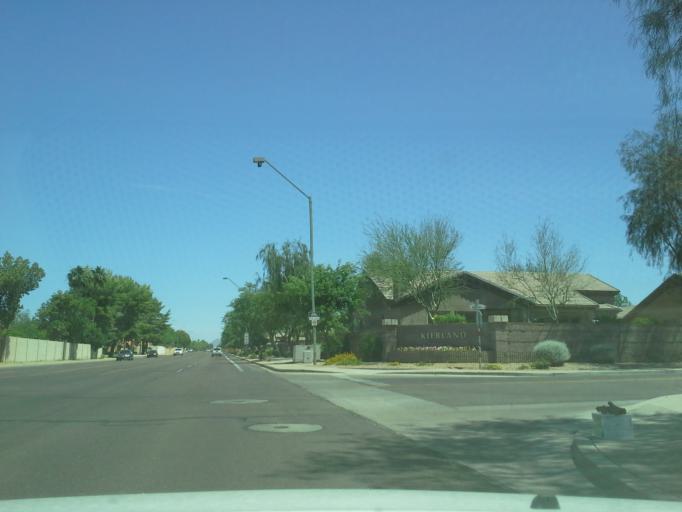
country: US
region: Arizona
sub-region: Maricopa County
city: Paradise Valley
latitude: 33.6185
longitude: -111.9430
